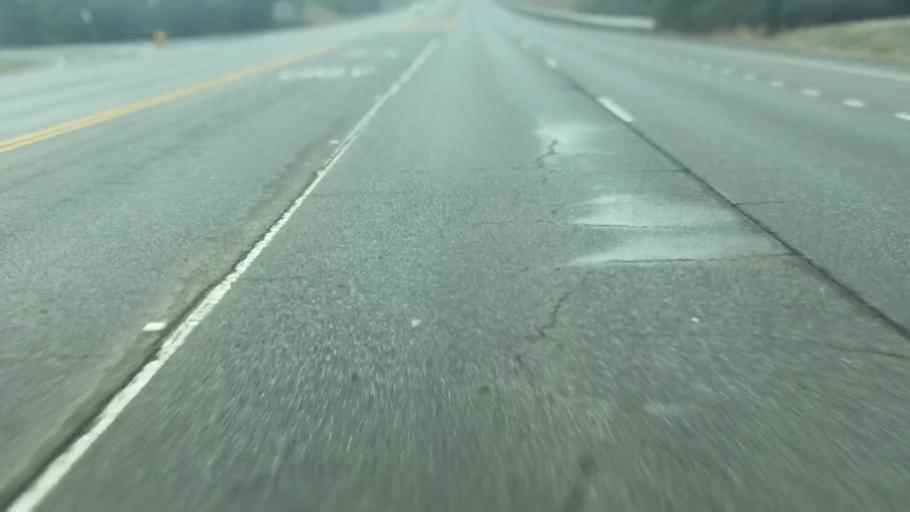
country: US
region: Alabama
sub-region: Walker County
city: Jasper
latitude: 33.8068
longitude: -87.2348
